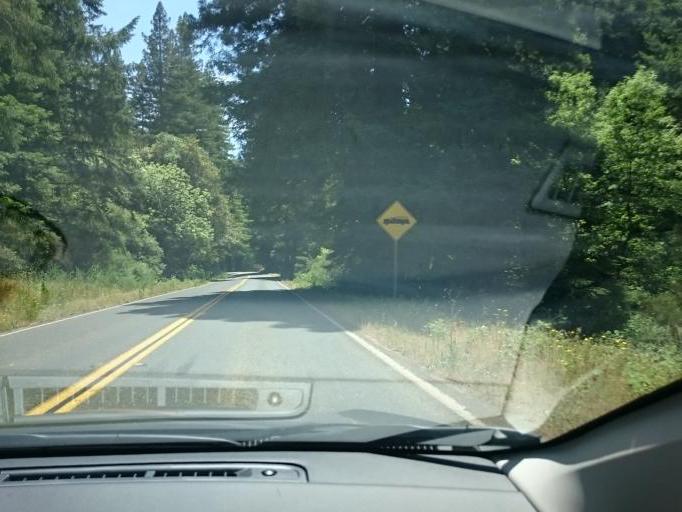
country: US
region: California
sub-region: Mendocino County
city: Boonville
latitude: 39.1545
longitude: -123.5465
